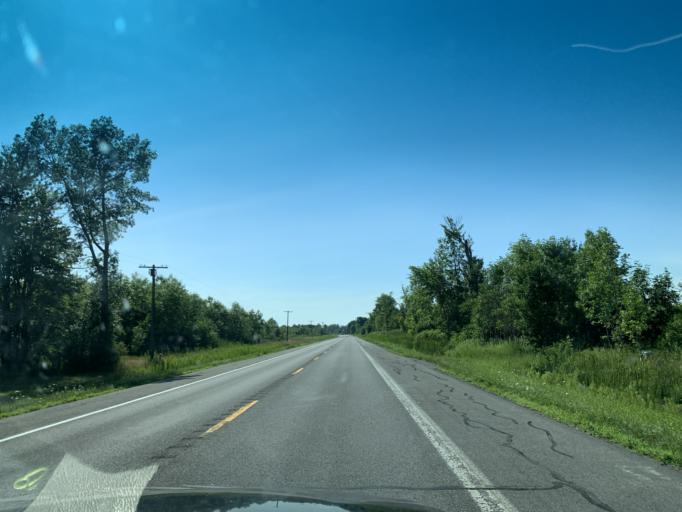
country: US
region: New York
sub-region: Madison County
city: Oneida
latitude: 43.1427
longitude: -75.6404
